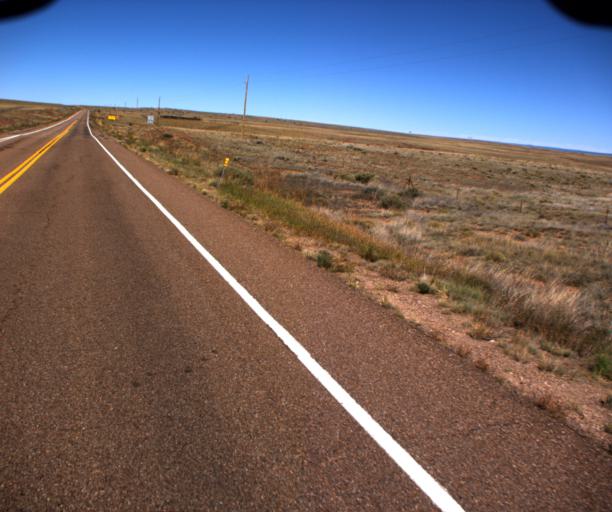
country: US
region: Arizona
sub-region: Apache County
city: Saint Johns
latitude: 34.5132
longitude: -109.4487
